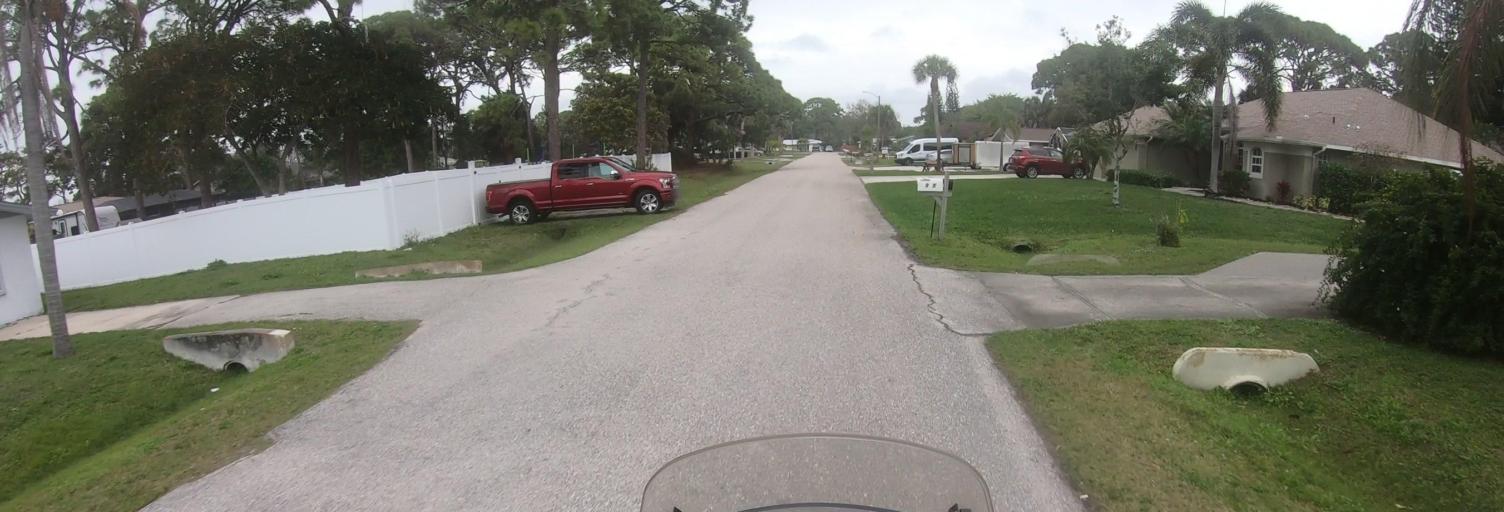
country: US
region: Florida
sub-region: Sarasota County
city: South Venice
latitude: 27.0591
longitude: -82.4270
